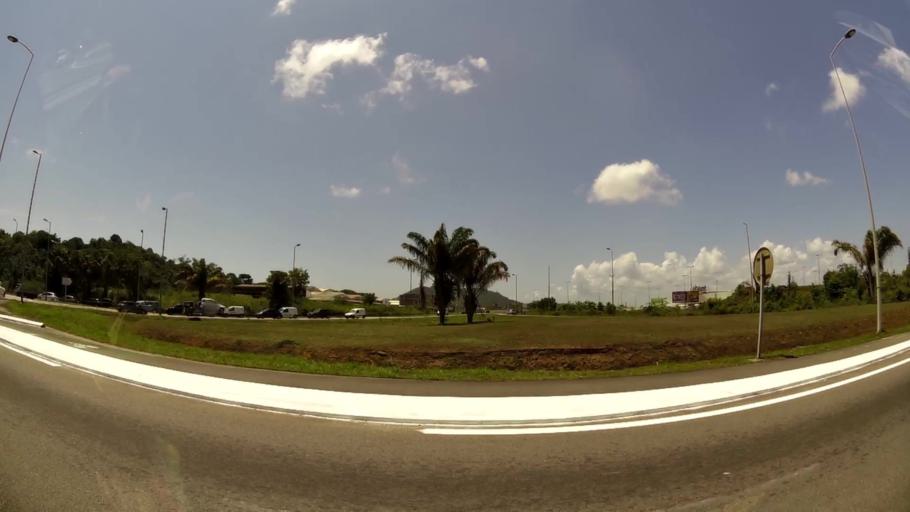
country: GF
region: Guyane
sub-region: Guyane
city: Cayenne
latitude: 4.9068
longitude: -52.3226
